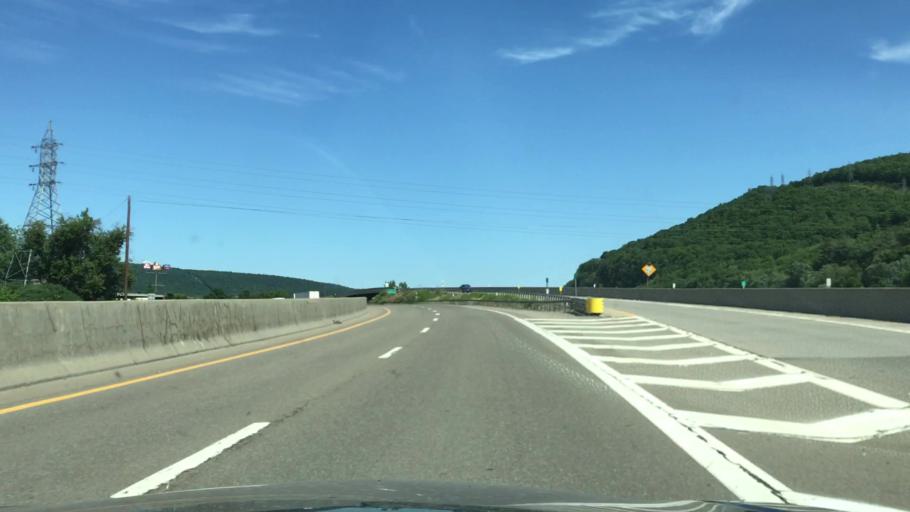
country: US
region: New York
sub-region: Steuben County
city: Painted Post
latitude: 42.1532
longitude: -77.0873
